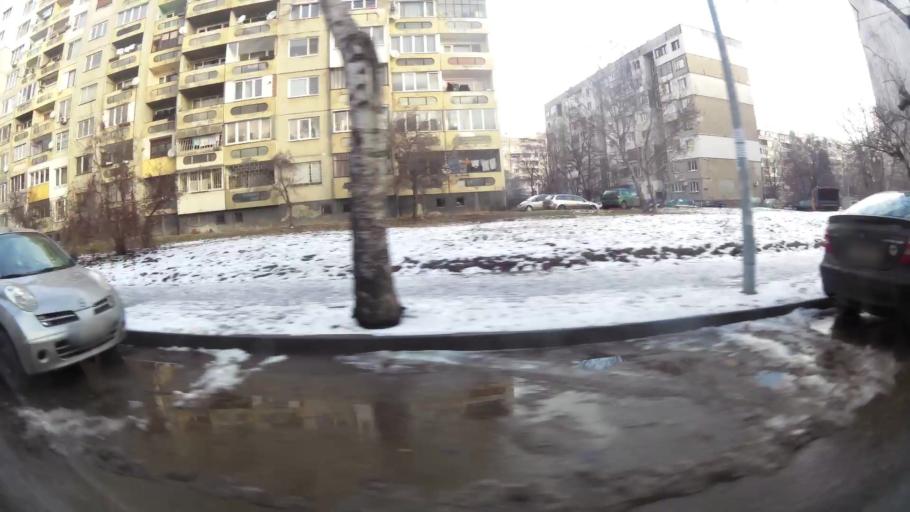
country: BG
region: Sofia-Capital
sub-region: Stolichna Obshtina
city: Sofia
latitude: 42.6968
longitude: 23.2825
